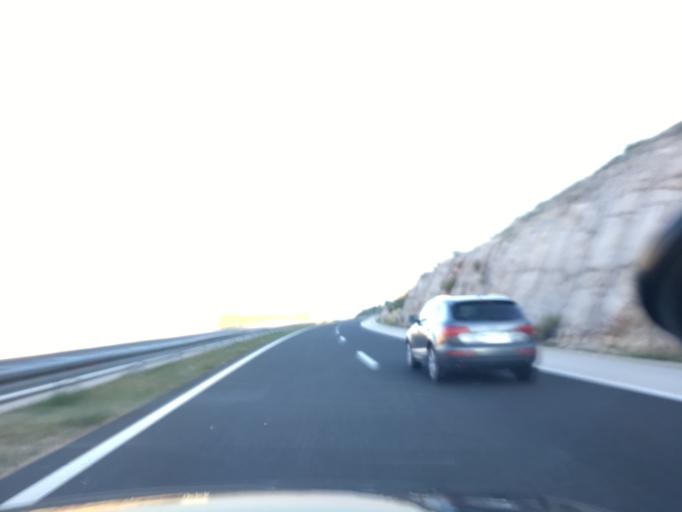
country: HR
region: Sibensko-Kniniska
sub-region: Grad Sibenik
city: Sibenik
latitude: 43.7550
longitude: 15.9434
